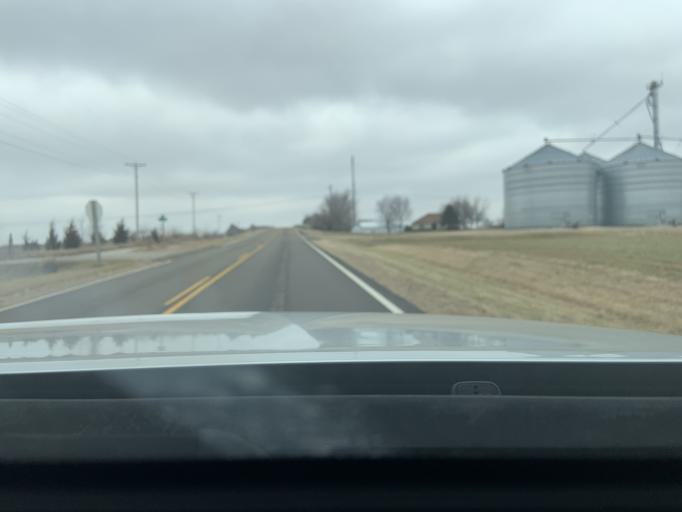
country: US
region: Illinois
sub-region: LaSalle County
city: Seneca
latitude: 41.3735
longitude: -88.6130
